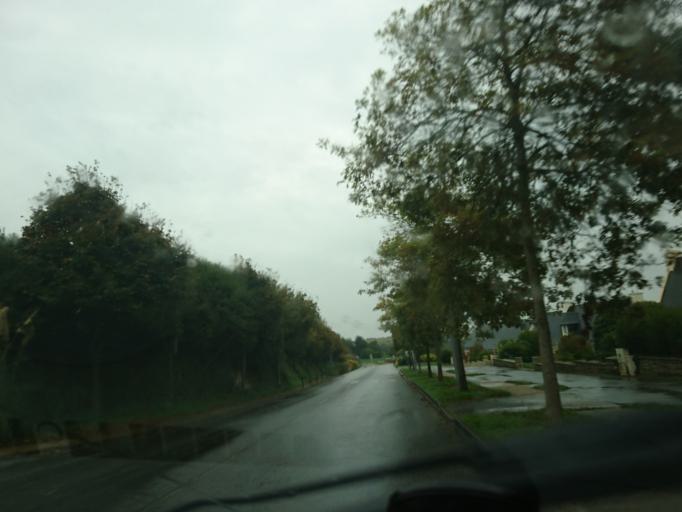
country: FR
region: Brittany
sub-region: Departement du Finistere
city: Plouguerneau
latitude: 48.6046
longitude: -4.5051
